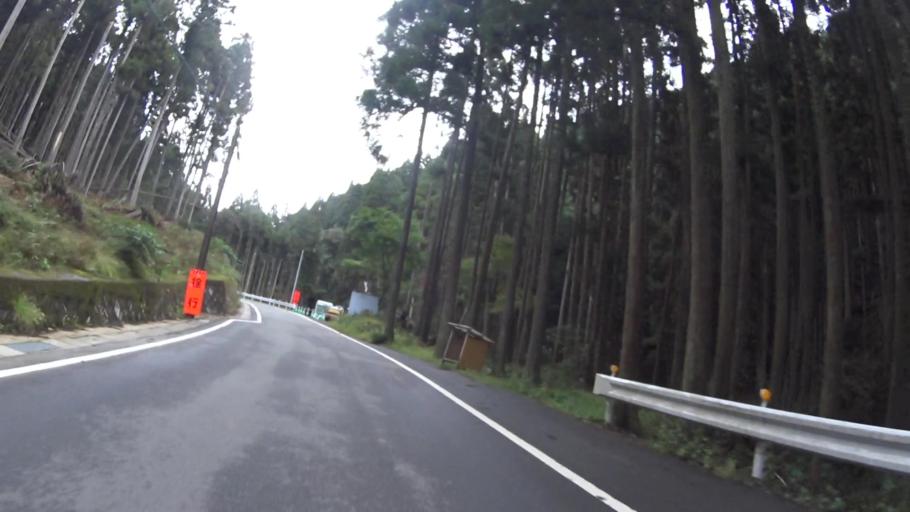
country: JP
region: Kyoto
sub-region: Kyoto-shi
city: Kamigyo-ku
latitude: 35.1356
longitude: 135.7783
